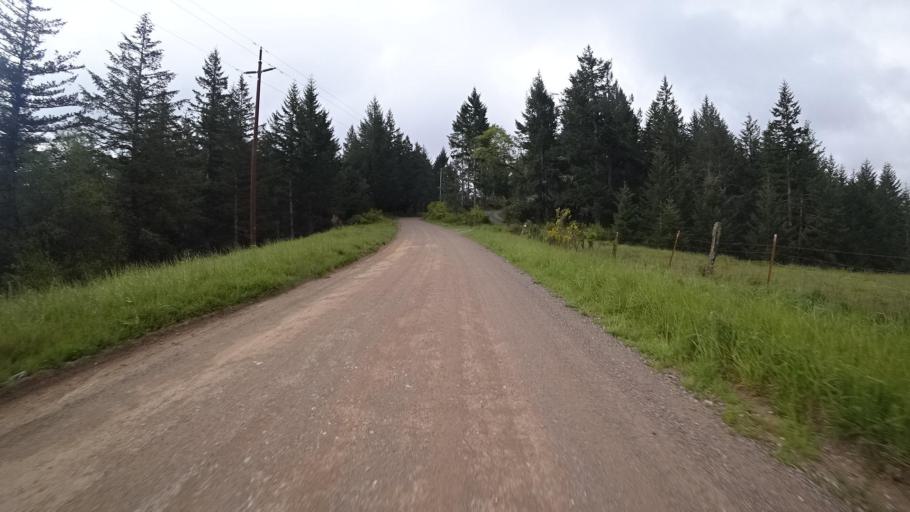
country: US
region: California
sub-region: Humboldt County
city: Redway
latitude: 40.2384
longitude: -123.7620
